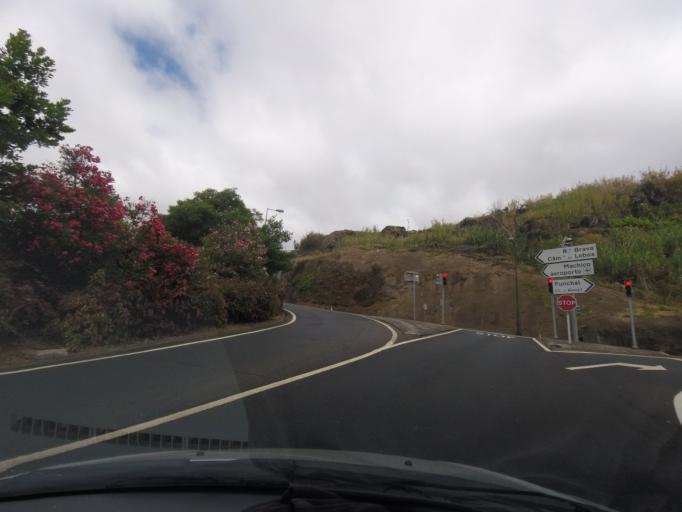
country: PT
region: Madeira
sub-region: Funchal
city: Nossa Senhora do Monte
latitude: 32.6618
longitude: -16.9020
